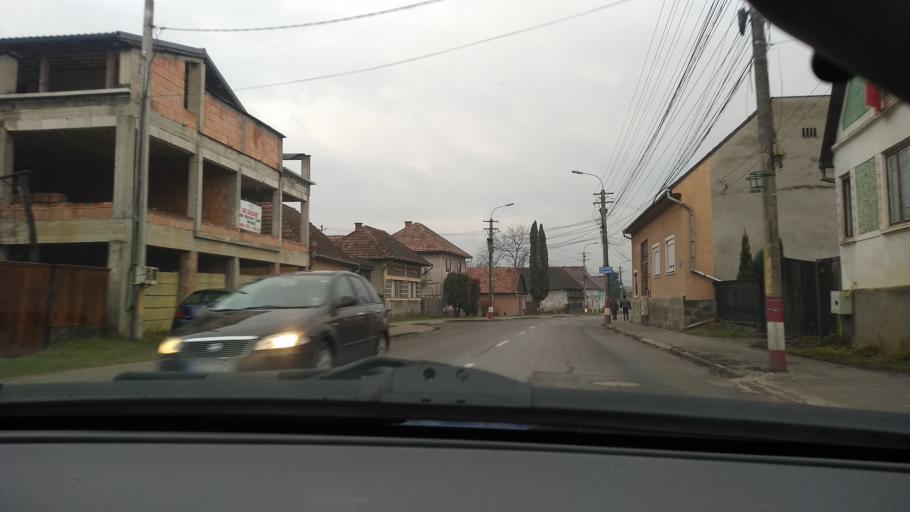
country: RO
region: Mures
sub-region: Oras Sovata
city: Sovata
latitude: 46.5894
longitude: 25.0689
